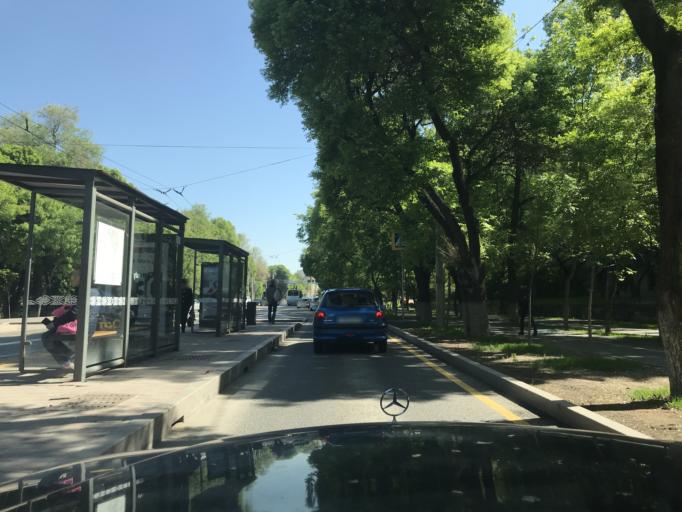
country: KZ
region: Almaty Qalasy
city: Almaty
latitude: 43.2279
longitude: 76.9297
